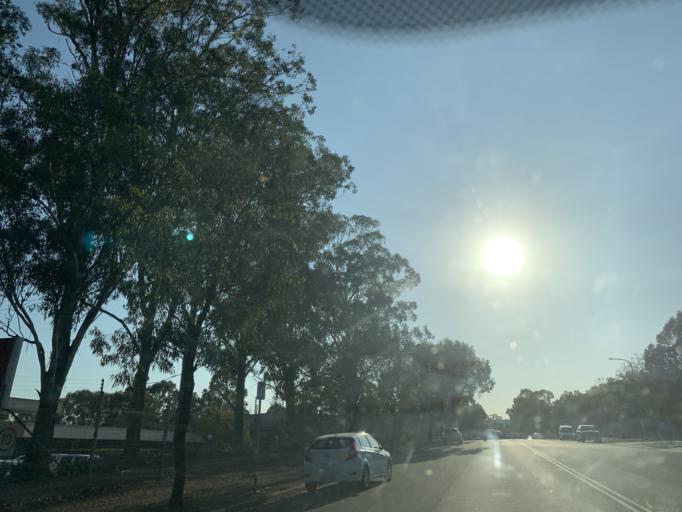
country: AU
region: New South Wales
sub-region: Blacktown
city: Doonside
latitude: -33.7979
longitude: 150.8839
